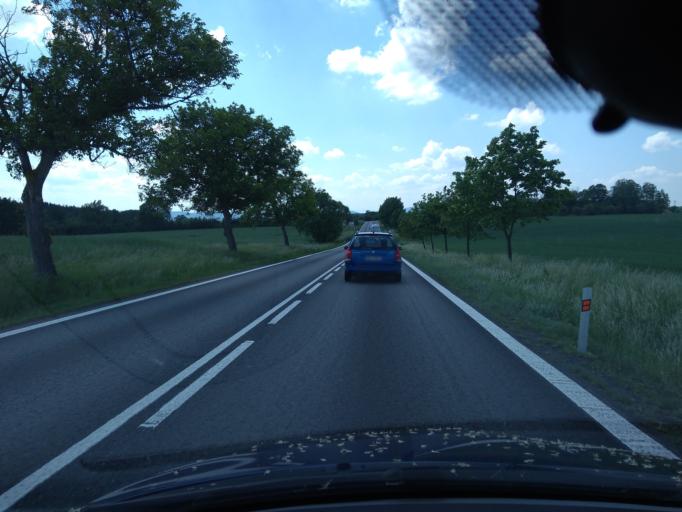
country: CZ
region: Plzensky
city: Chlumcany
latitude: 49.6211
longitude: 13.3274
